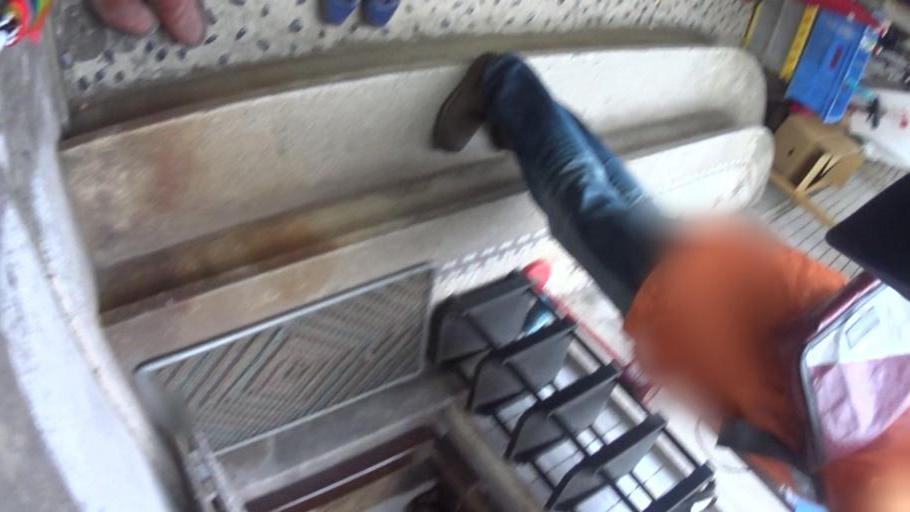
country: JP
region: Aichi
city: Nagoya-shi
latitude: 35.1195
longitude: 136.9051
